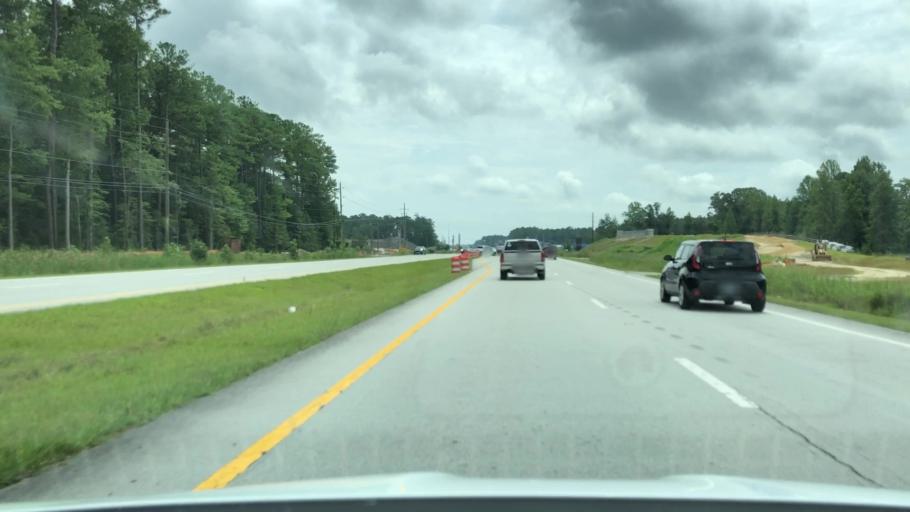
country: US
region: North Carolina
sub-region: Craven County
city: Neuse Forest
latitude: 34.9209
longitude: -76.9438
